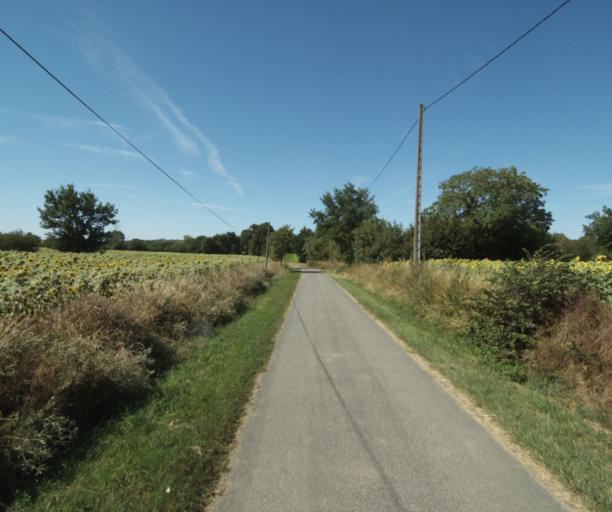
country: FR
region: Midi-Pyrenees
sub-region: Departement de la Haute-Garonne
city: Saint-Felix-Lauragais
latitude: 43.5061
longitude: 1.8921
